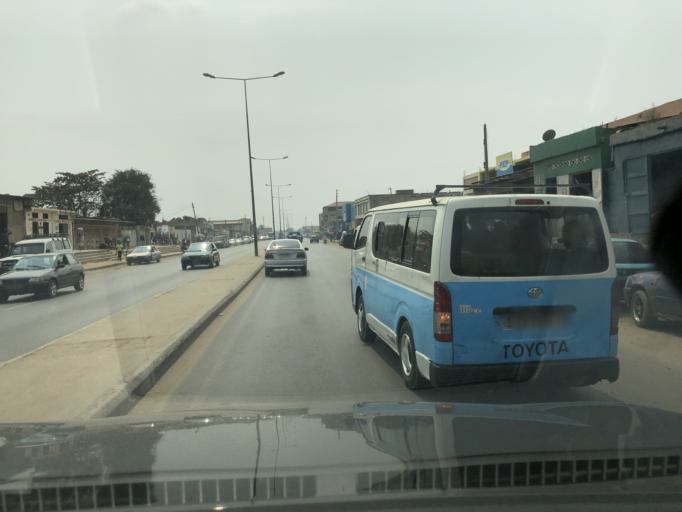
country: AO
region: Luanda
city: Luanda
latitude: -8.8025
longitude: 13.3082
